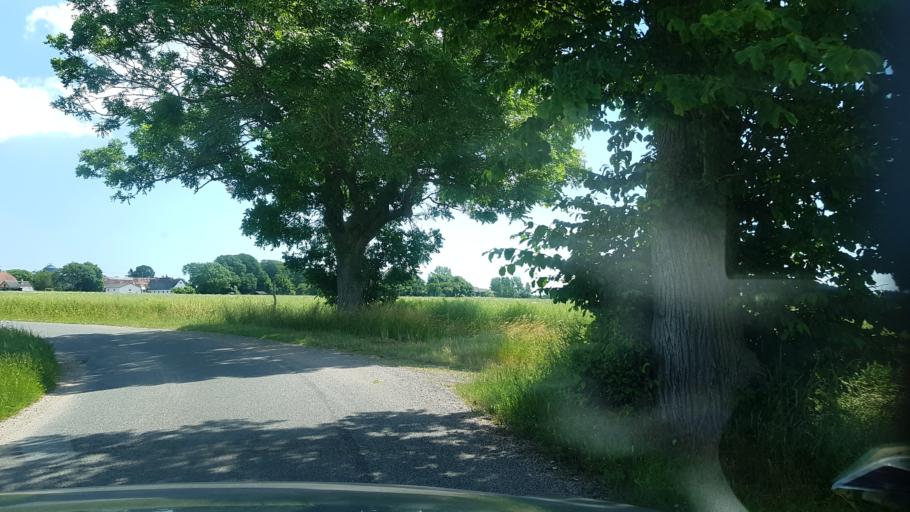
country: DK
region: Zealand
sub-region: Kalundborg Kommune
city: Svebolle
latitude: 55.7020
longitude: 11.2885
